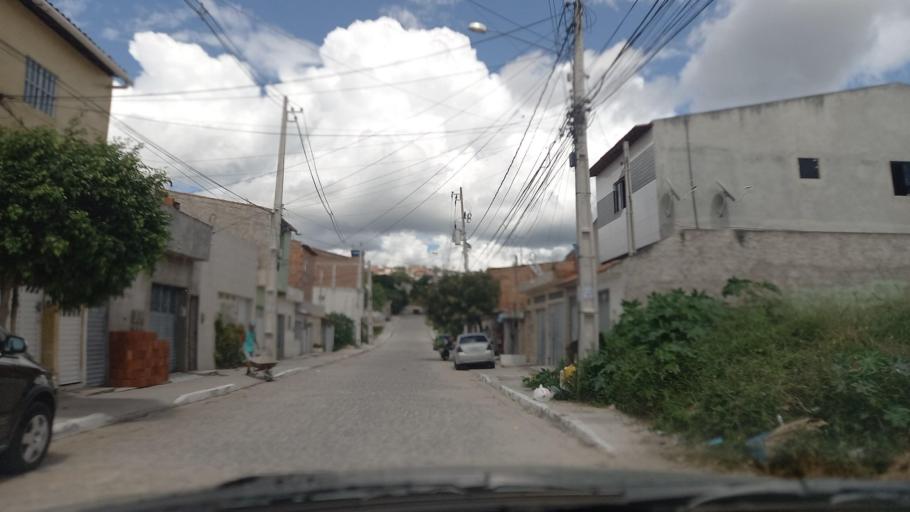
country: BR
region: Pernambuco
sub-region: Caruaru
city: Caruaru
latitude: -8.3013
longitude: -35.9757
